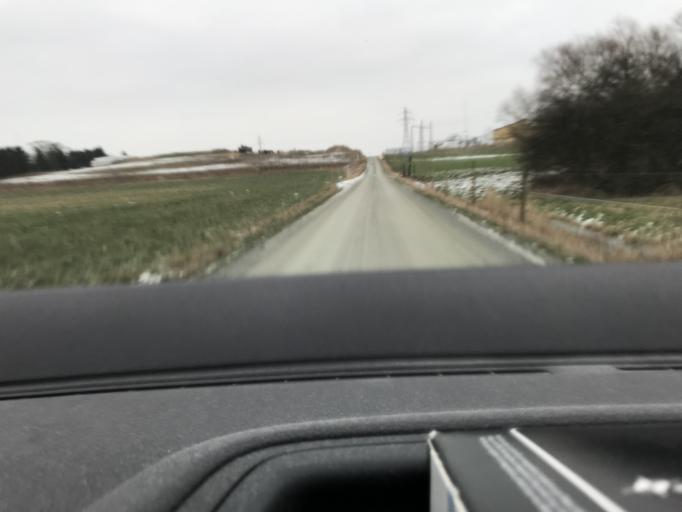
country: SE
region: Skane
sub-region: Ystads Kommun
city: Kopingebro
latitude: 55.4592
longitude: 13.8907
